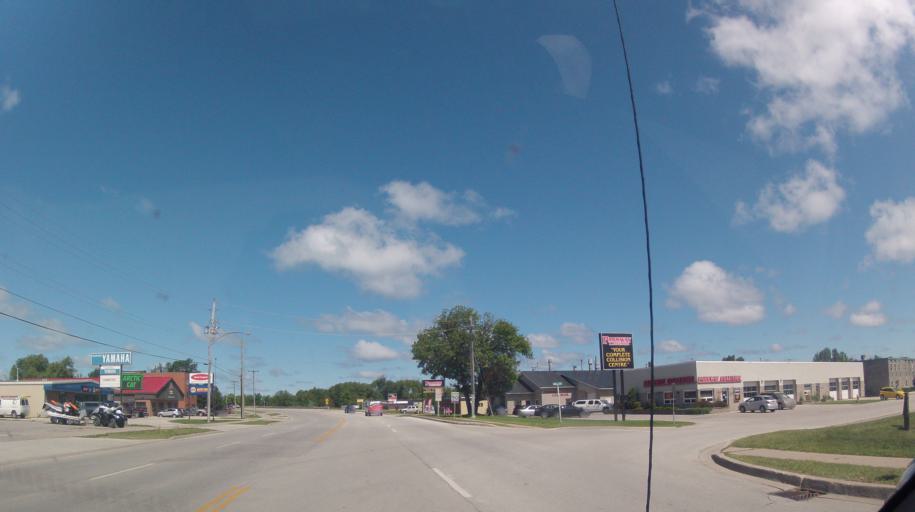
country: CA
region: Ontario
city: Collingwood
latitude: 44.5008
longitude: -80.1965
